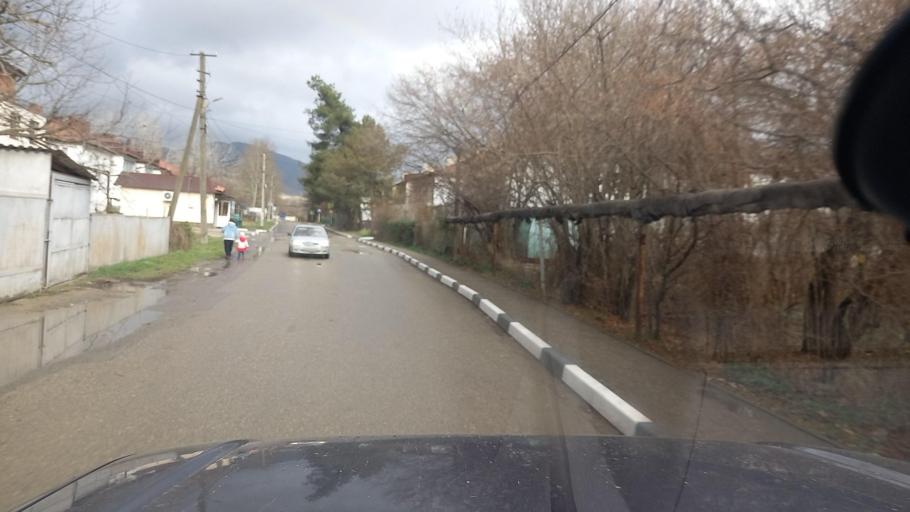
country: RU
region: Krasnodarskiy
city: Pshada
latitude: 44.4747
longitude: 38.3985
